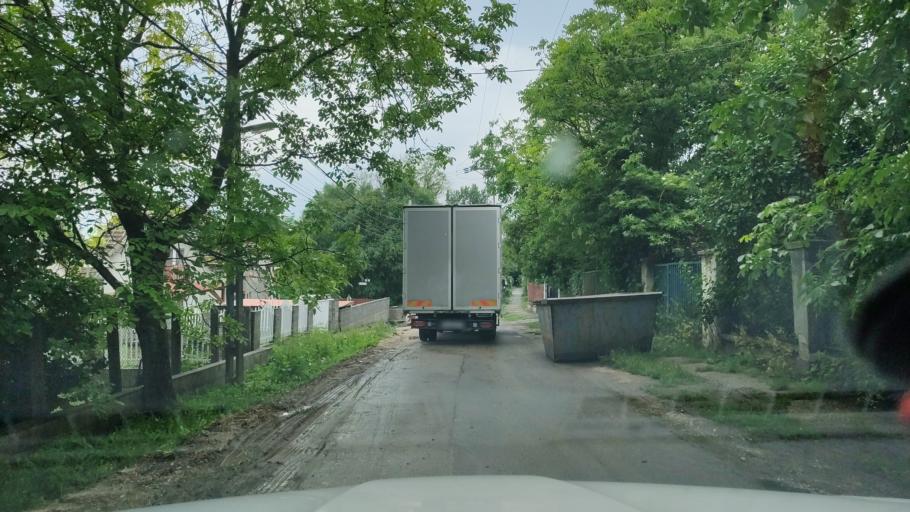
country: HU
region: Pest
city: Toeroekbalint
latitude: 47.4365
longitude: 18.9201
